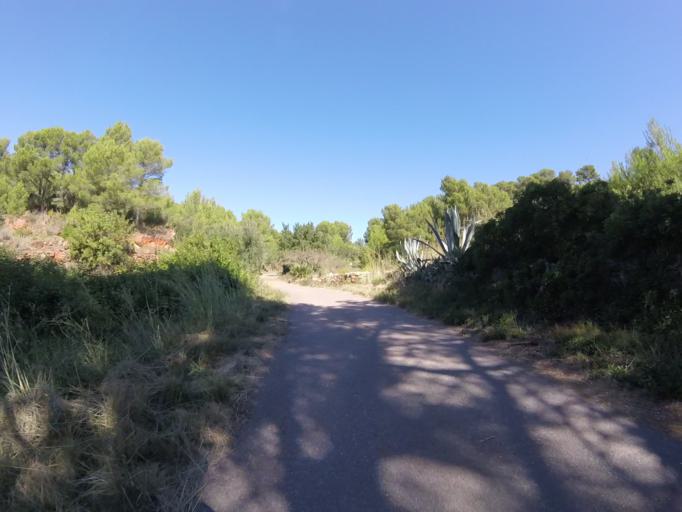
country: ES
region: Valencia
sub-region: Provincia de Castello
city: Cabanes
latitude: 40.1410
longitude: 0.1024
